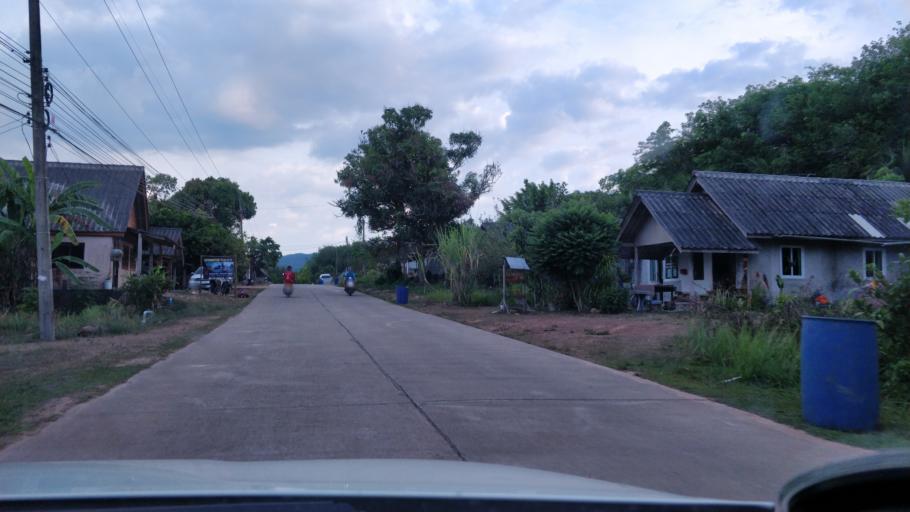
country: TH
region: Krabi
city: Saladan
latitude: 7.5896
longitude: 99.0686
